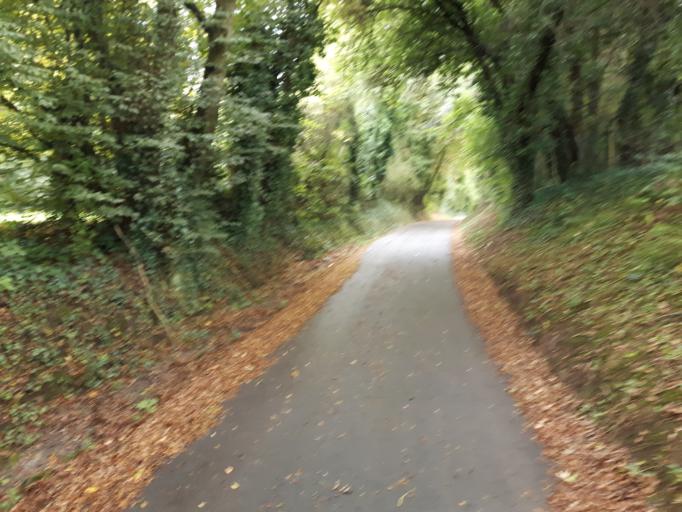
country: DE
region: Baden-Wuerttemberg
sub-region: Karlsruhe Region
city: Maulbronn
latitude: 49.0037
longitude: 8.8134
